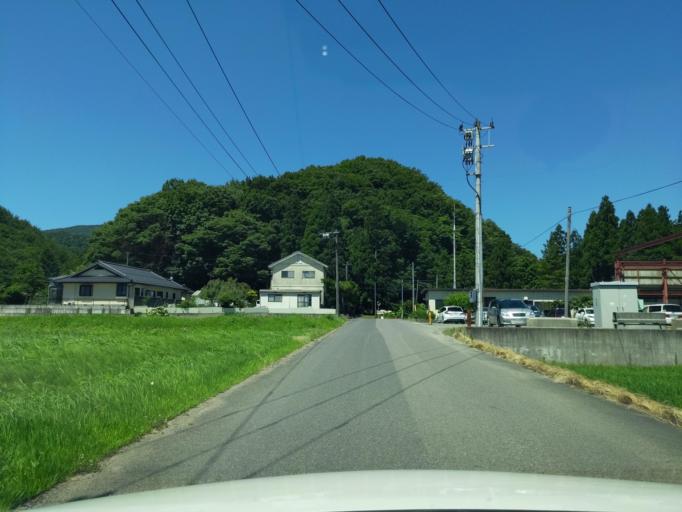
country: JP
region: Fukushima
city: Koriyama
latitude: 37.3896
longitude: 140.2408
